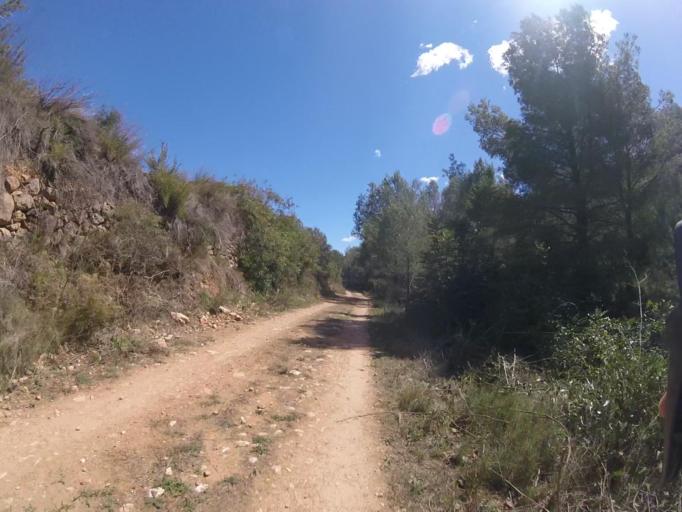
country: ES
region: Valencia
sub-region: Provincia de Castello
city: Orpesa/Oropesa del Mar
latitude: 40.1669
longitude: 0.1309
